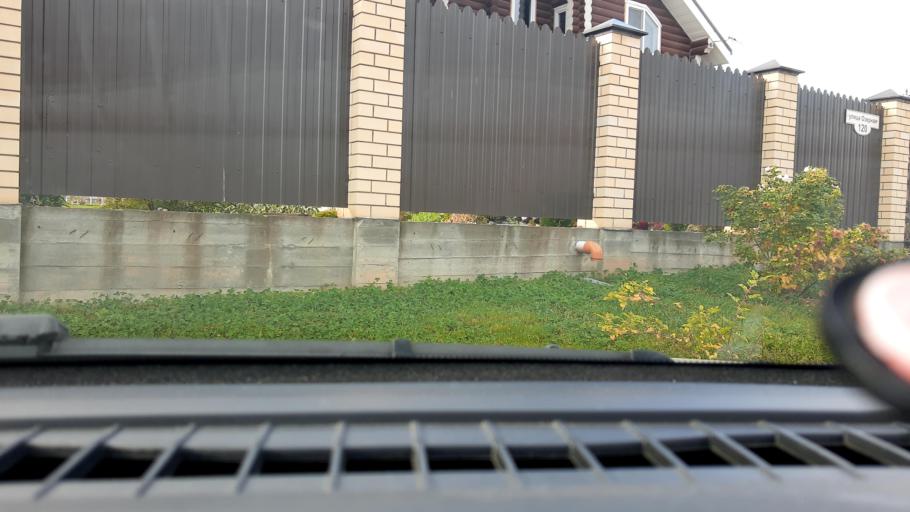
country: RU
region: Nizjnij Novgorod
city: Afonino
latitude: 56.1979
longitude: 44.0883
